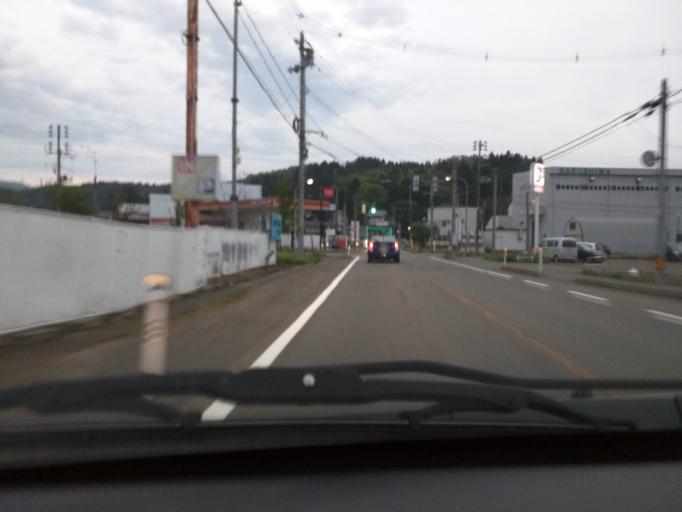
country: JP
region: Niigata
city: Ojiya
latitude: 37.3220
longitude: 138.7143
